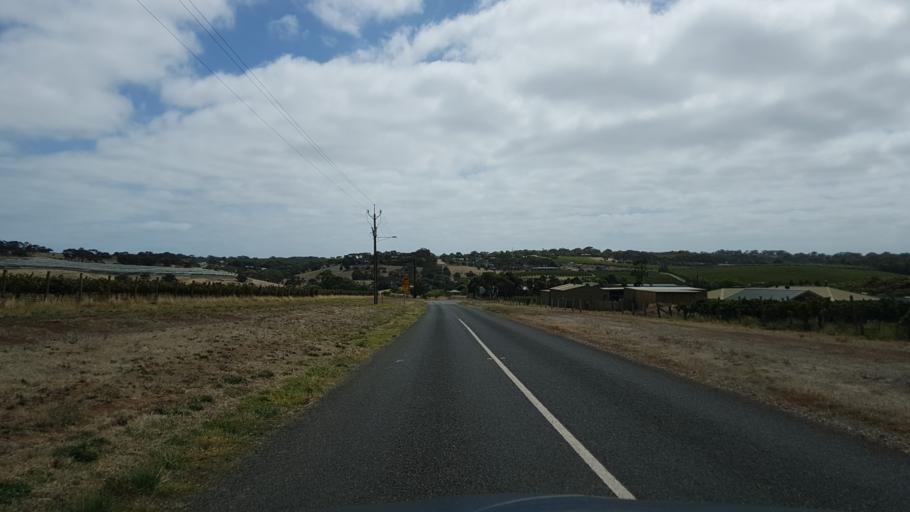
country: AU
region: South Australia
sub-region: Onkaparinga
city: McLaren Vale
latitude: -35.2123
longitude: 138.5175
